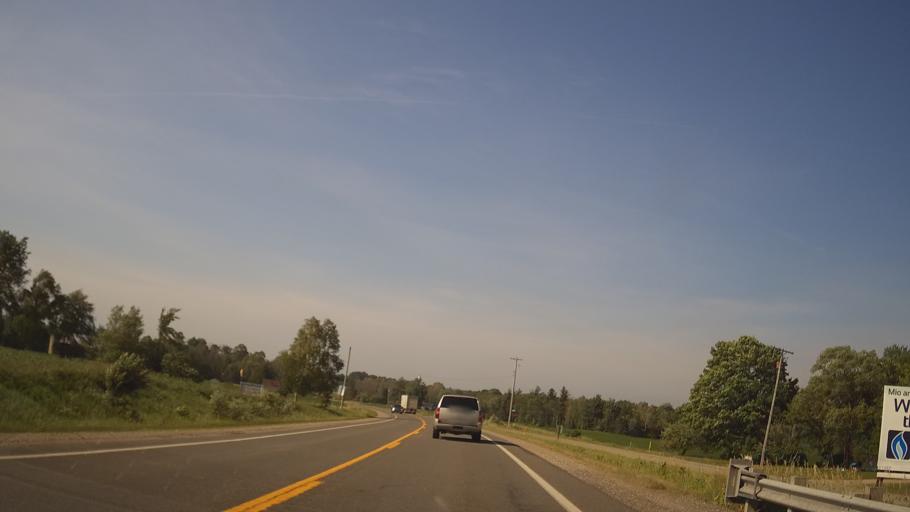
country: US
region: Michigan
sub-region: Ogemaw County
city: West Branch
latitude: 44.3699
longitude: -84.1163
